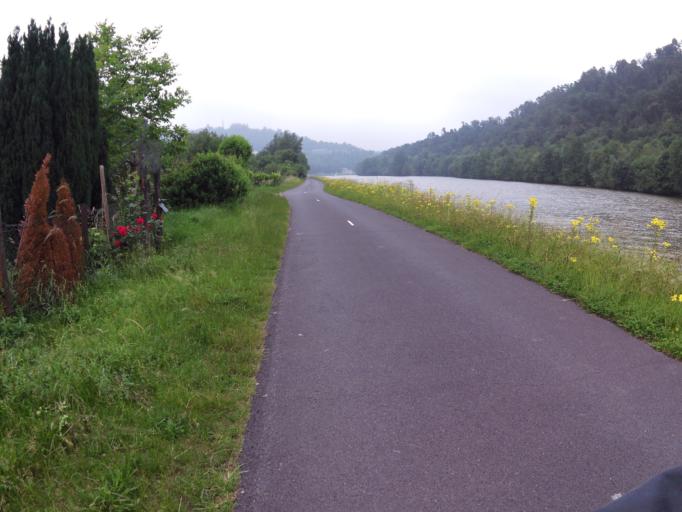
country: FR
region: Champagne-Ardenne
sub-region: Departement des Ardennes
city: Fumay
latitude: 49.9817
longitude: 4.6917
